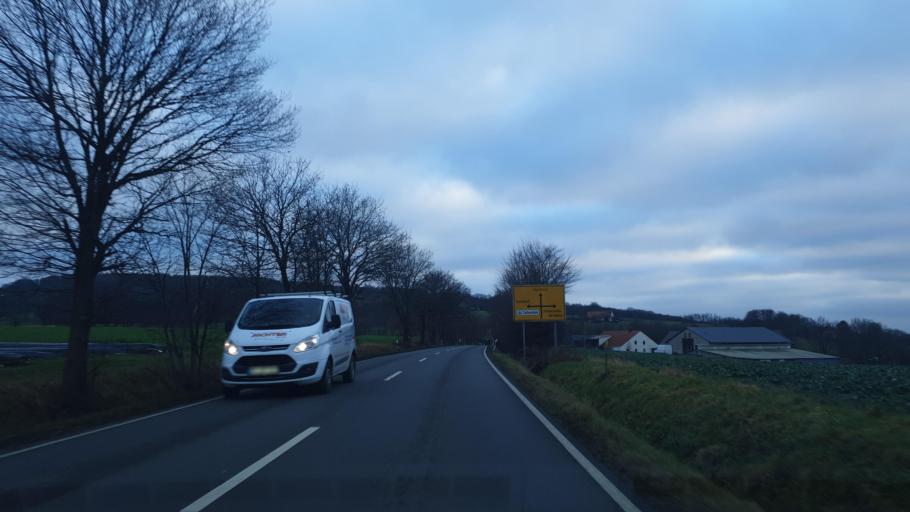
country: DE
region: North Rhine-Westphalia
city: Loehne
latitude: 52.1626
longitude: 8.6844
